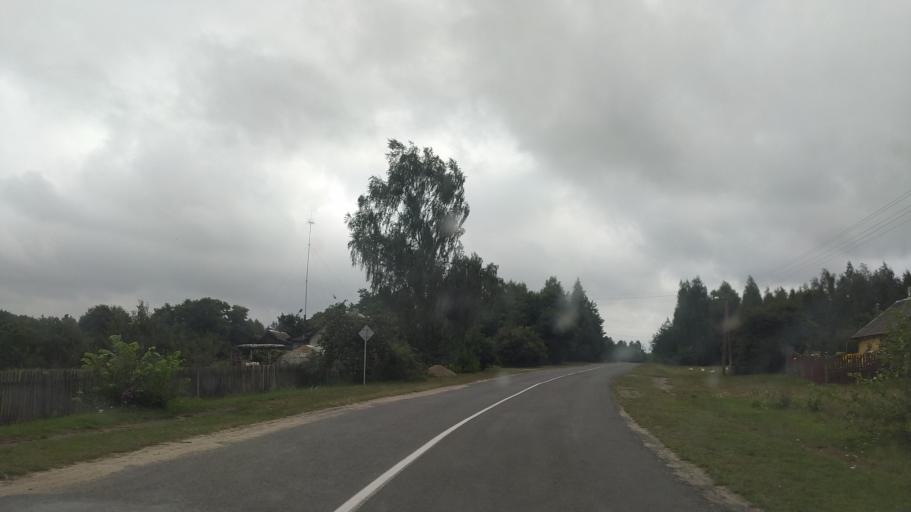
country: BY
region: Brest
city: Byaroza
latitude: 52.5957
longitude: 24.8710
